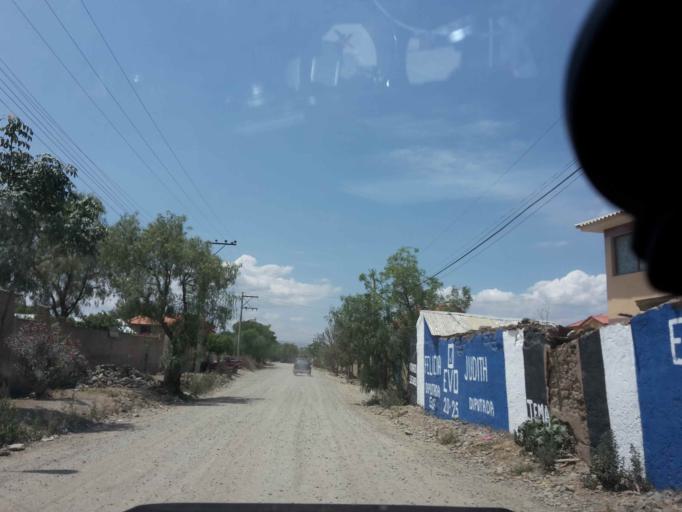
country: BO
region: Cochabamba
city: Cochabamba
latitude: -17.3331
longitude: -66.2194
